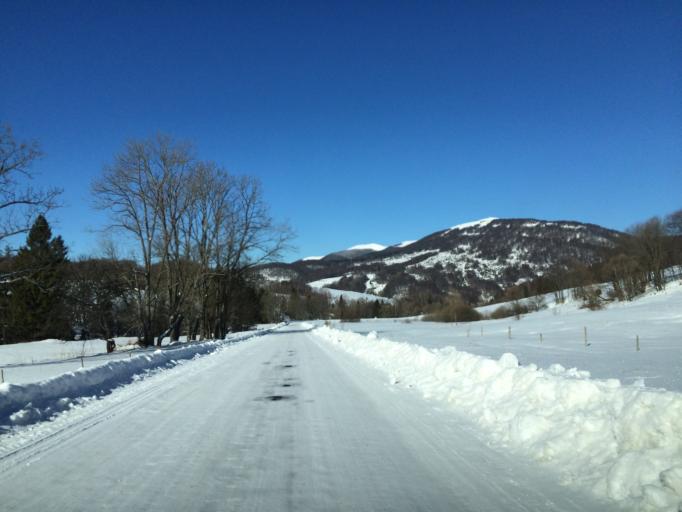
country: PL
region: Subcarpathian Voivodeship
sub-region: Powiat bieszczadzki
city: Lutowiska
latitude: 49.1302
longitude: 22.5798
